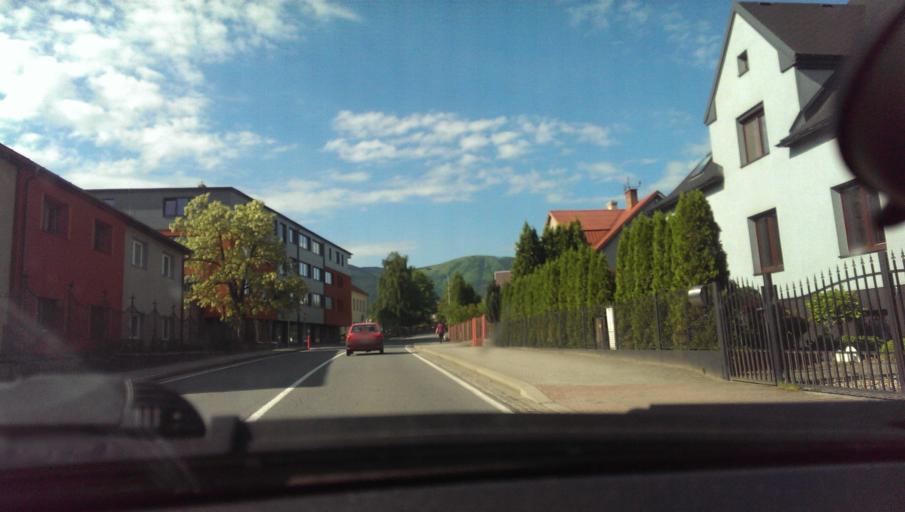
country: CZ
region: Moravskoslezsky
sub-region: Okres Frydek-Mistek
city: Celadna
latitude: 49.5477
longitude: 18.3372
